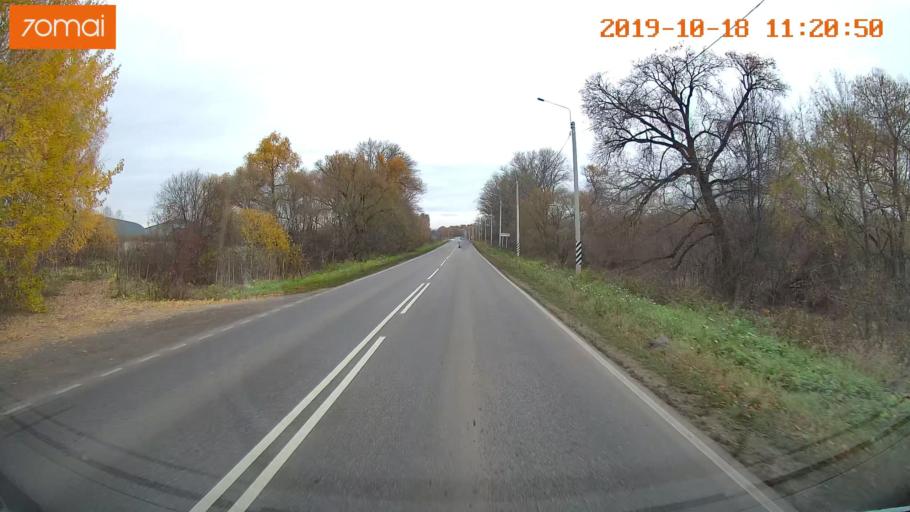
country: RU
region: Tula
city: Kimovsk
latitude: 54.0666
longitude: 38.5608
